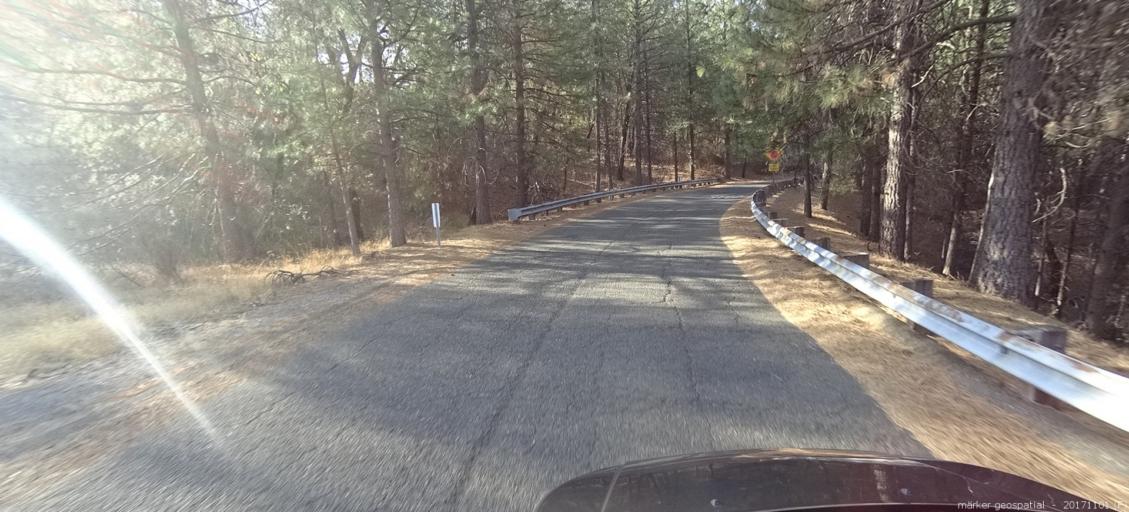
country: US
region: California
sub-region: Shasta County
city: Shasta Lake
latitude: 40.7902
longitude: -122.3242
